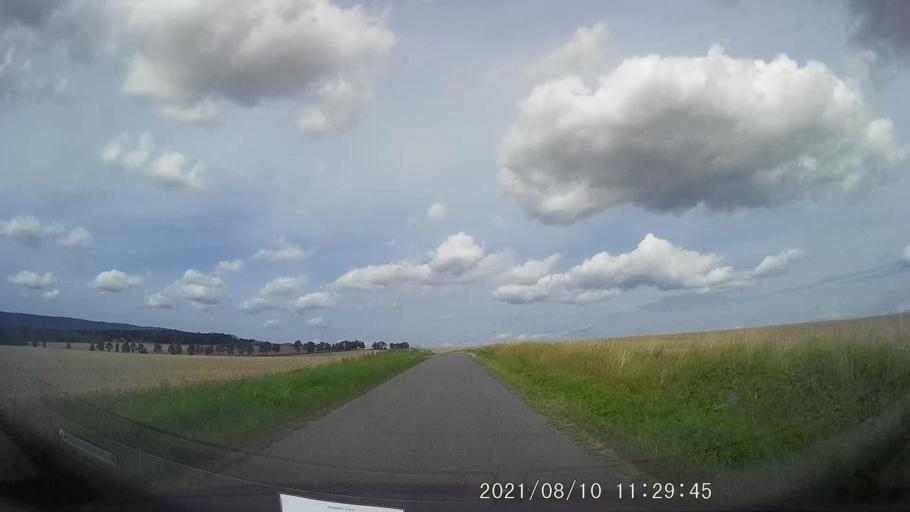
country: PL
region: Lower Silesian Voivodeship
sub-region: Powiat klodzki
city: Polanica-Zdroj
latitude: 50.4461
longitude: 16.5593
